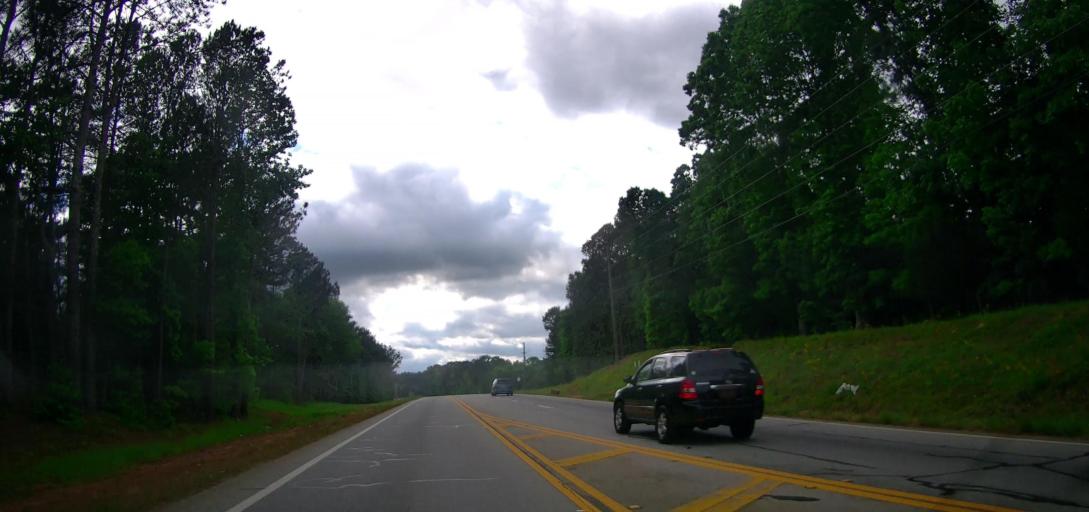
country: US
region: Georgia
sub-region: Walton County
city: Walnut Grove
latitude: 33.7533
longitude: -83.8269
